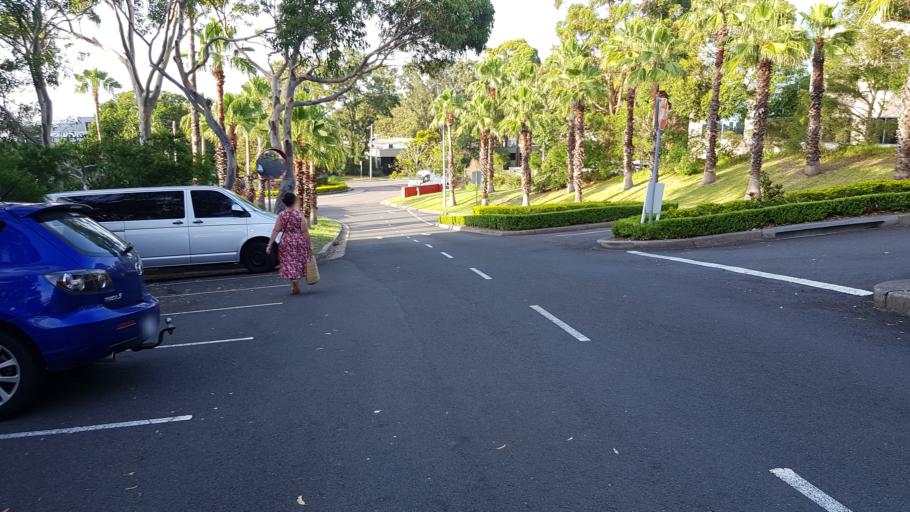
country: AU
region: New South Wales
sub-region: Warringah
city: Allambie Heights
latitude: -33.7535
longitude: 151.2483
